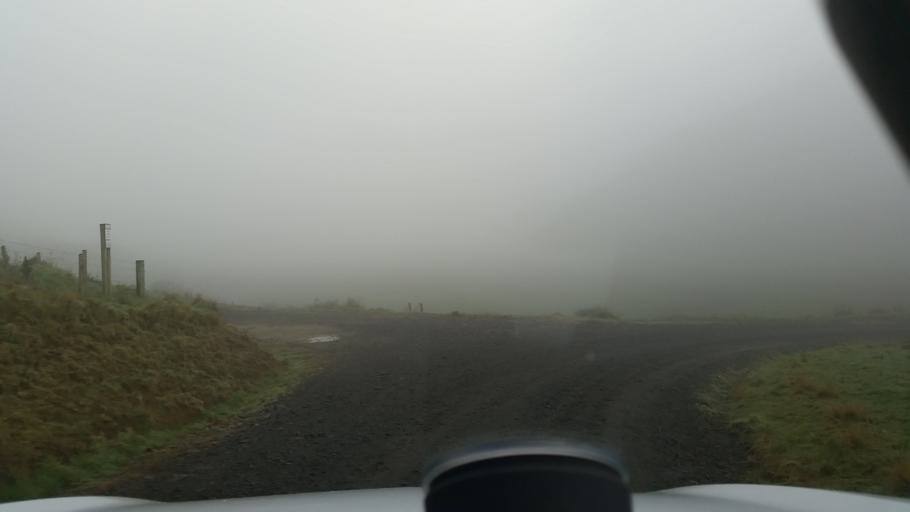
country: NZ
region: Taranaki
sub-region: South Taranaki District
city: Eltham
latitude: -39.4109
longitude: 174.4255
